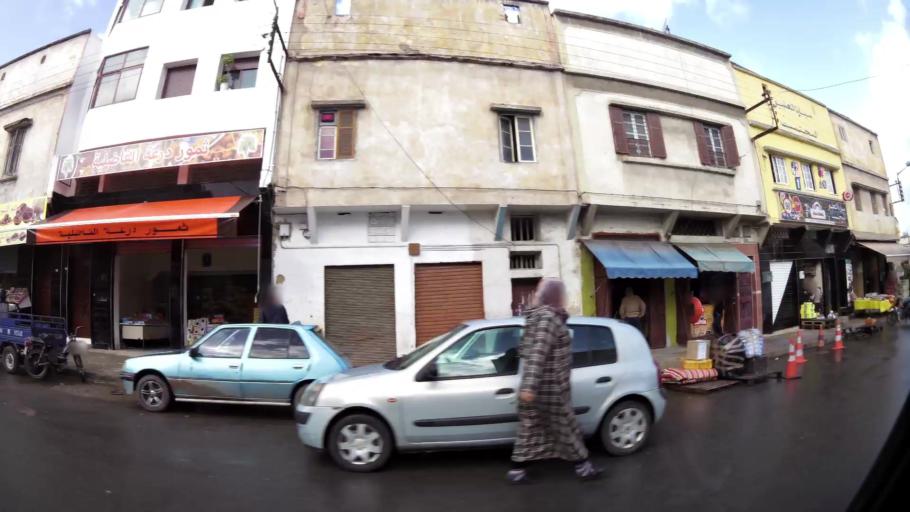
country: MA
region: Grand Casablanca
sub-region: Casablanca
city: Casablanca
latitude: 33.5674
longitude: -7.5819
